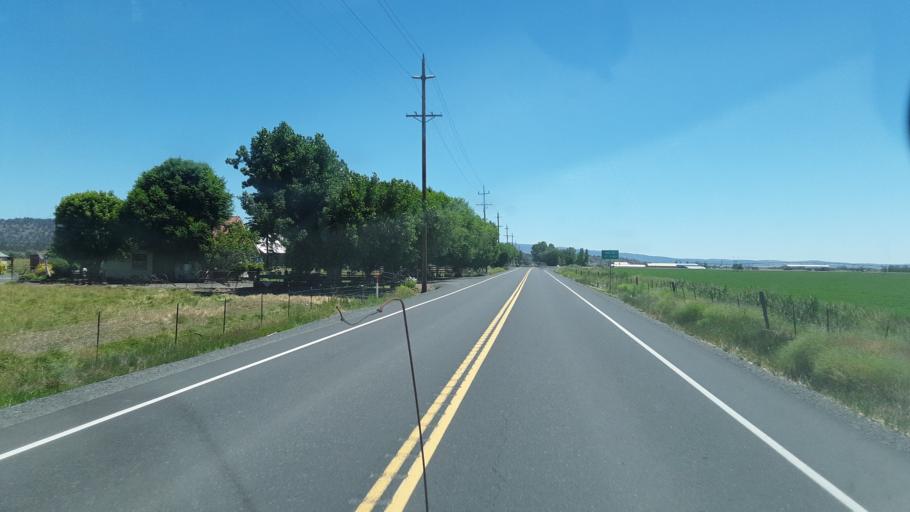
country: US
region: California
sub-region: Siskiyou County
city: Tulelake
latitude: 42.0241
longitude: -121.5568
